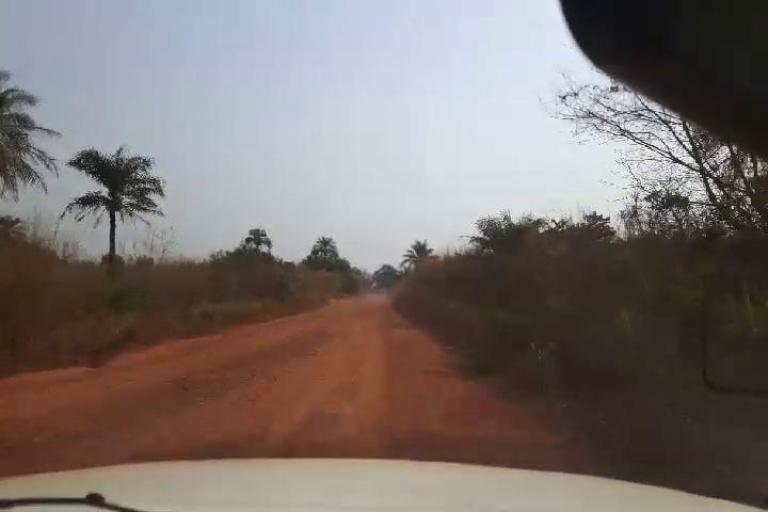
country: SL
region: Northern Province
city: Masingbi
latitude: 8.8504
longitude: -11.8279
